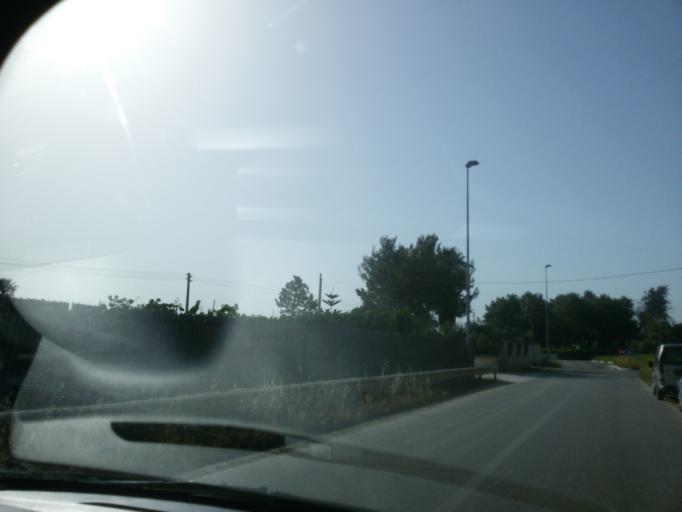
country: IT
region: Apulia
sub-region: Provincia di Brindisi
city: Mesagne
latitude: 40.5429
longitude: 17.8159
